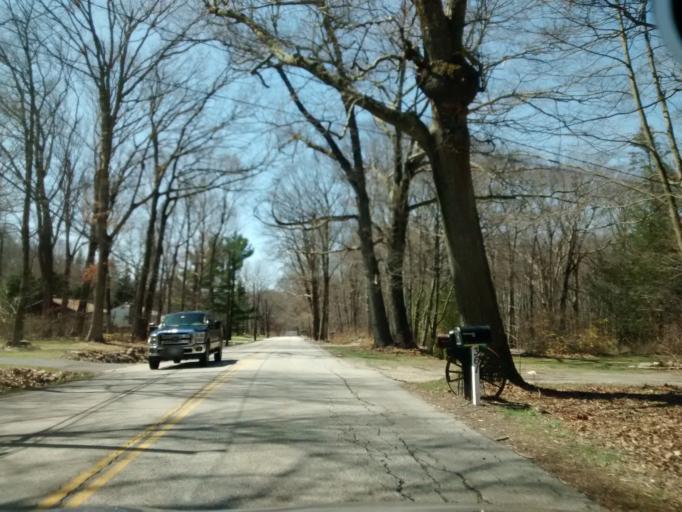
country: US
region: Massachusetts
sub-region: Worcester County
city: Sutton
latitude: 42.1353
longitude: -71.7528
